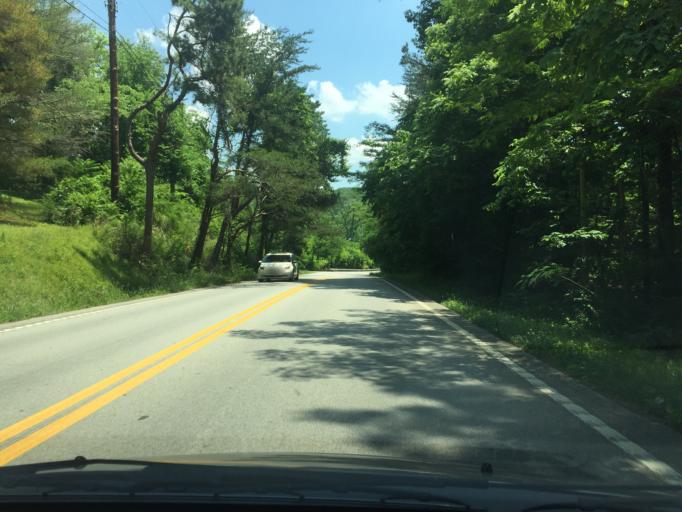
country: US
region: Tennessee
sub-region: Hamilton County
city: Lookout Mountain
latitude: 35.0239
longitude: -85.3913
